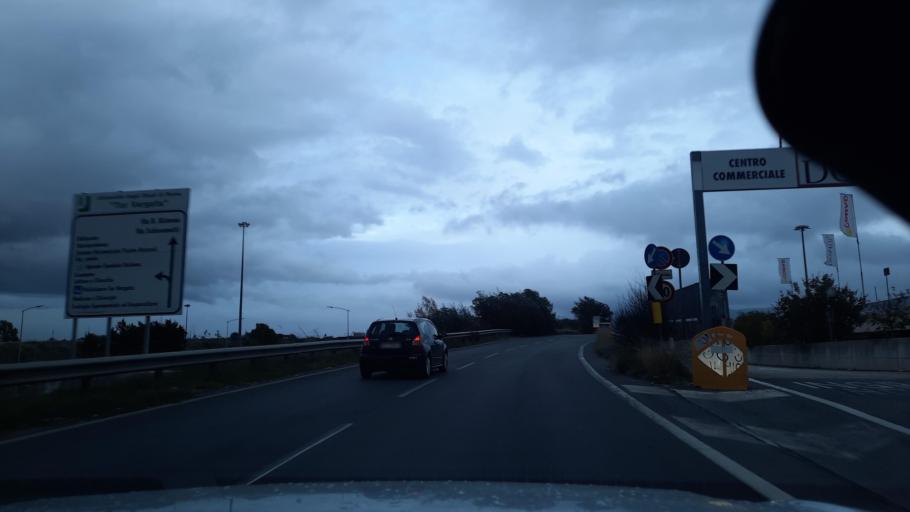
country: IT
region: Latium
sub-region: Citta metropolitana di Roma Capitale
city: Ciampino
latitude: 41.8485
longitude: 12.6090
